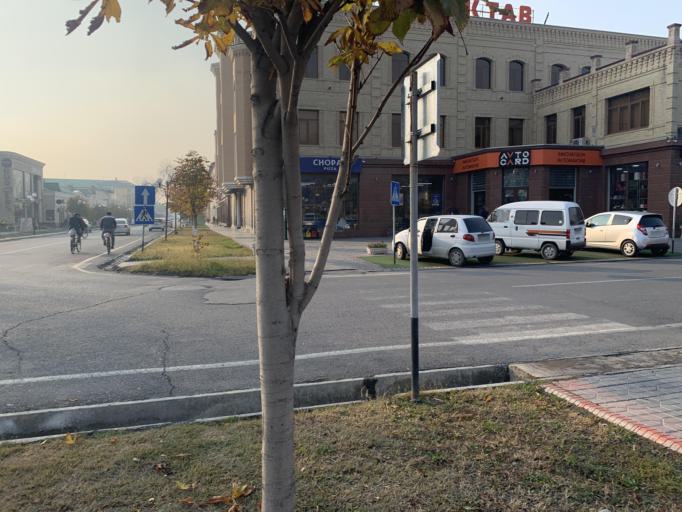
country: UZ
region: Fergana
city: Qo`qon
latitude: 40.5371
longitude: 70.9346
